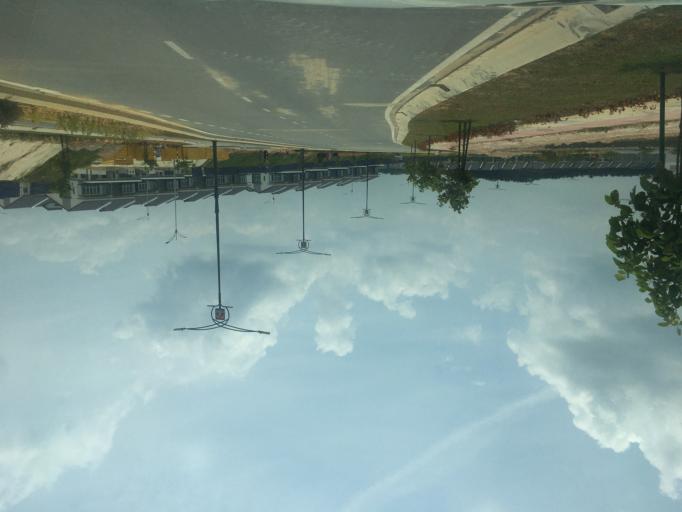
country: MY
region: Putrajaya
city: Putrajaya
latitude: 2.8537
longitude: 101.7054
